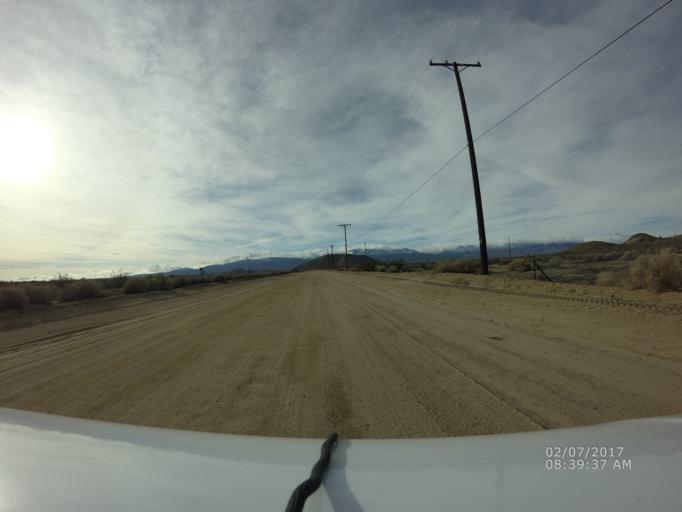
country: US
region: California
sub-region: Los Angeles County
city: Lake Los Angeles
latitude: 34.5883
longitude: -117.7203
